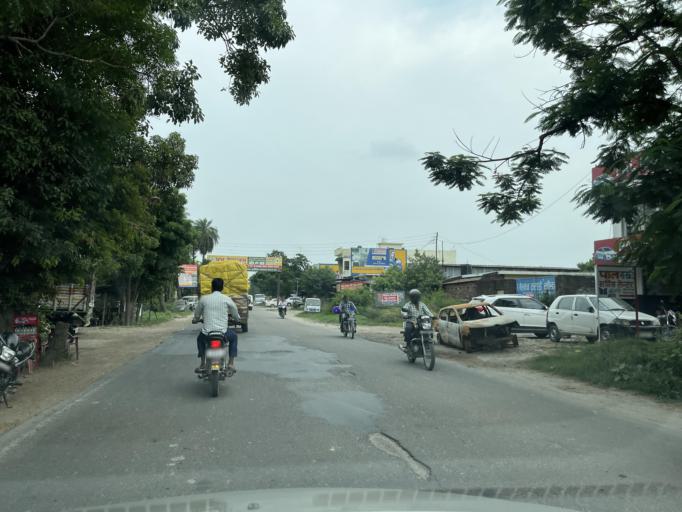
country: IN
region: Uttar Pradesh
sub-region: Rampur
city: Bilaspur
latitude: 29.0373
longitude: 79.2543
